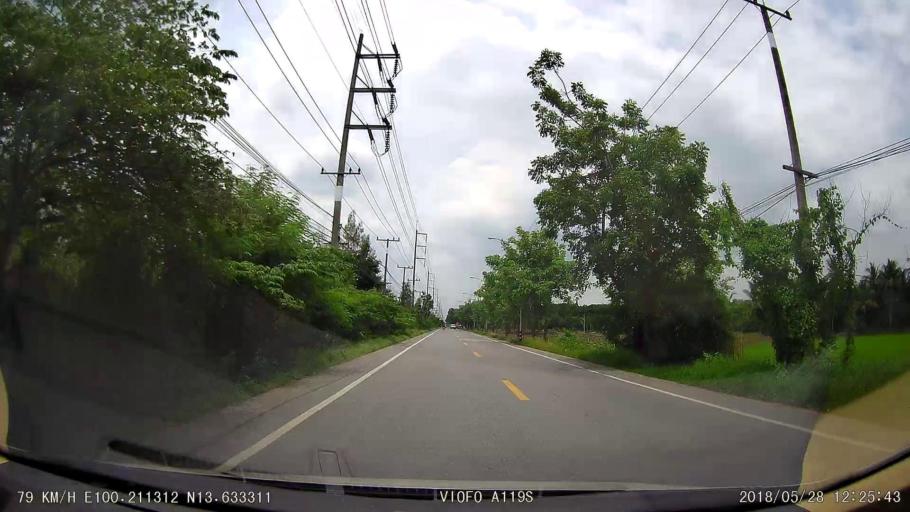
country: TH
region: Samut Sakhon
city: Krathum Baen
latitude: 13.6375
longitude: 100.2254
